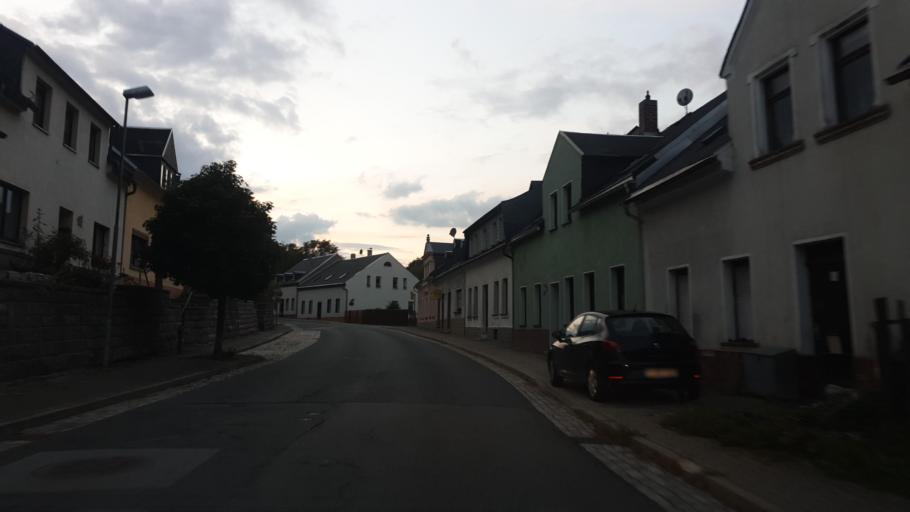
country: DE
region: Saxony
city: Eibenstock
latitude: 50.4975
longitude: 12.5896
